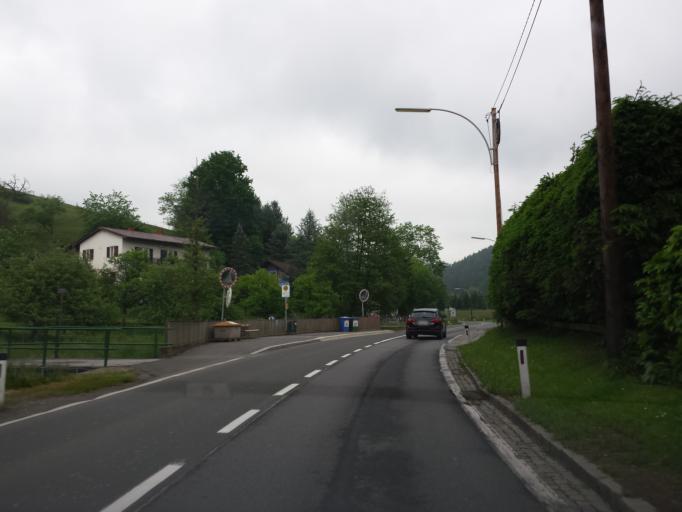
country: AT
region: Styria
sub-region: Politischer Bezirk Graz-Umgebung
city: Stattegg
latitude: 47.1207
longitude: 15.4384
